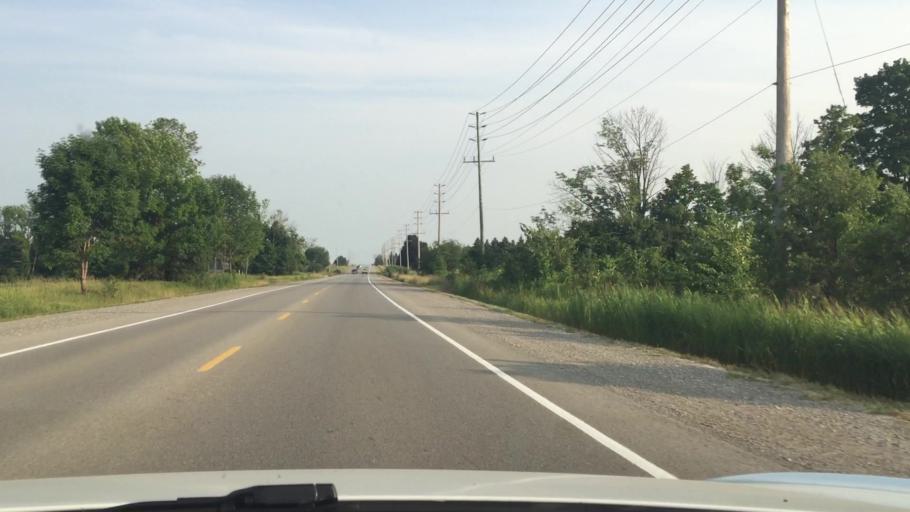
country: CA
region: Ontario
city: Oshawa
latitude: 43.8937
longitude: -78.7701
